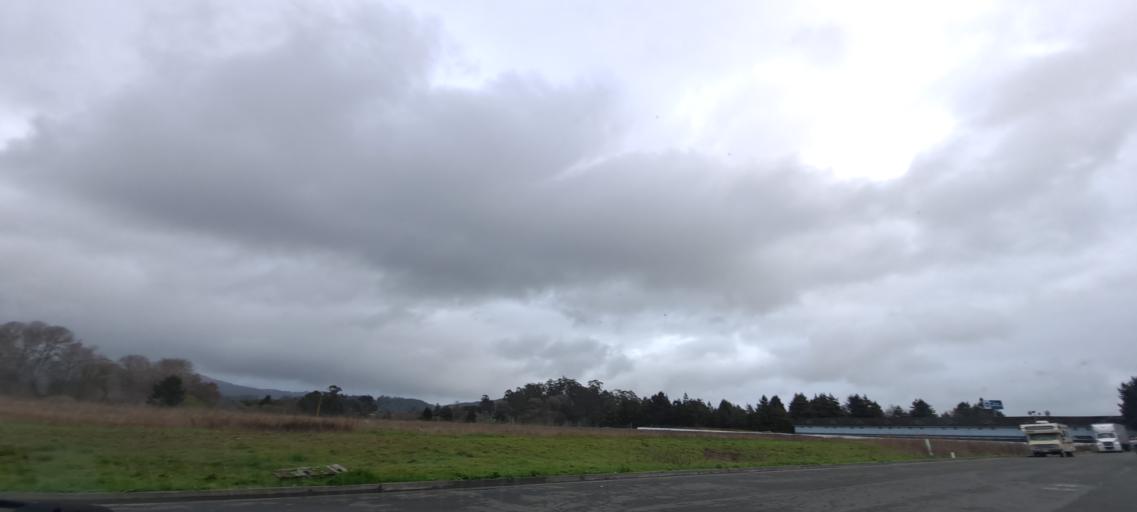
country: US
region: California
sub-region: Humboldt County
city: Fortuna
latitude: 40.5791
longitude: -124.1524
